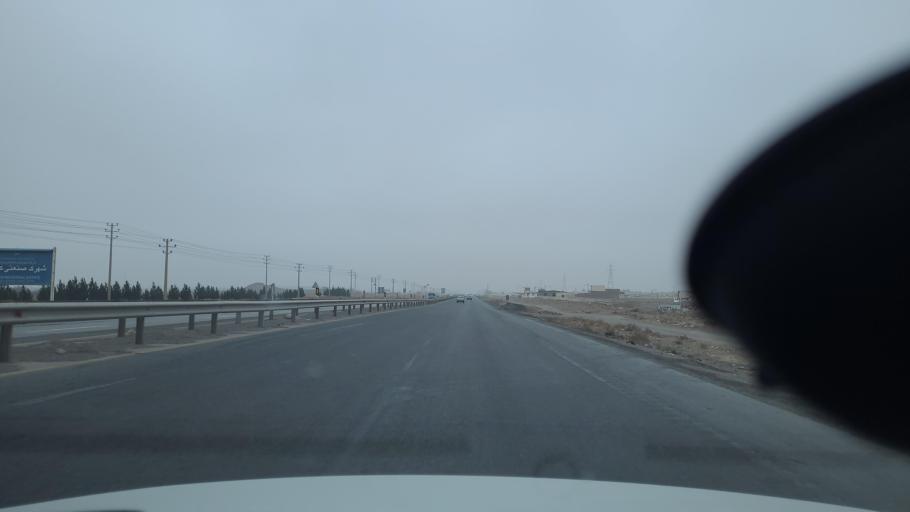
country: IR
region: Razavi Khorasan
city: Fariman
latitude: 35.9357
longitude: 59.7513
